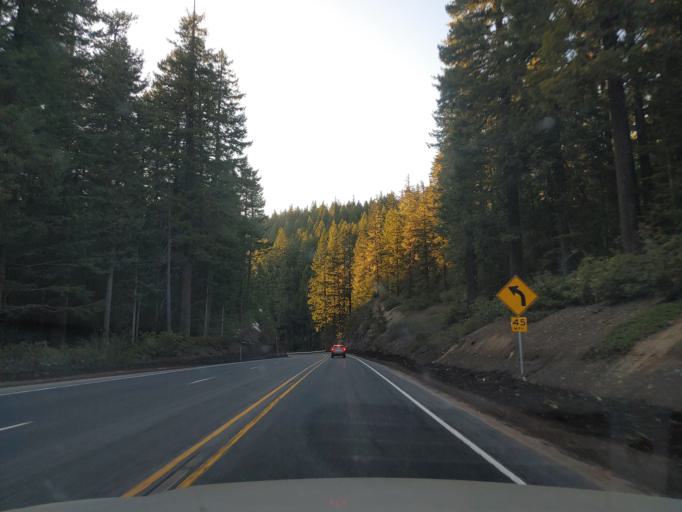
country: US
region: Oregon
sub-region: Lane County
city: Oakridge
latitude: 43.6123
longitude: -122.1255
